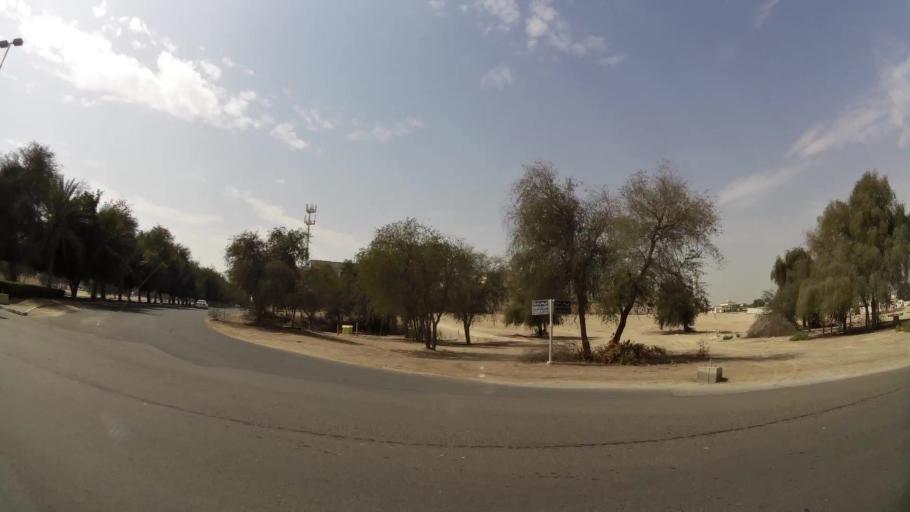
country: AE
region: Abu Dhabi
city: Abu Dhabi
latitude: 24.3072
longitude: 54.6180
